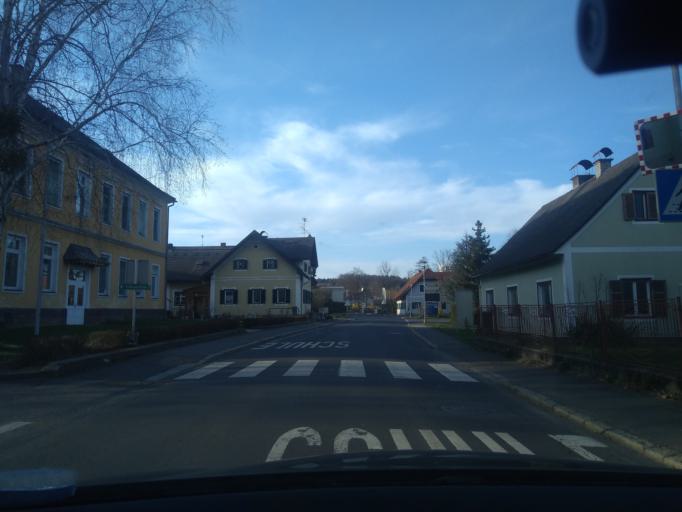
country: AT
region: Styria
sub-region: Politischer Bezirk Suedoststeiermark
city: Sankt Peter am Ottersbach
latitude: 46.8006
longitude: 15.7590
